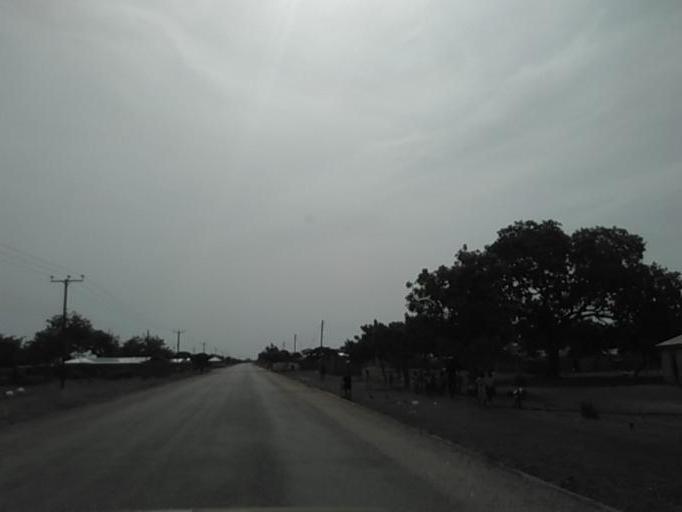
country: GH
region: Northern
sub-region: Yendi
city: Yendi
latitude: 9.4350
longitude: -0.1746
